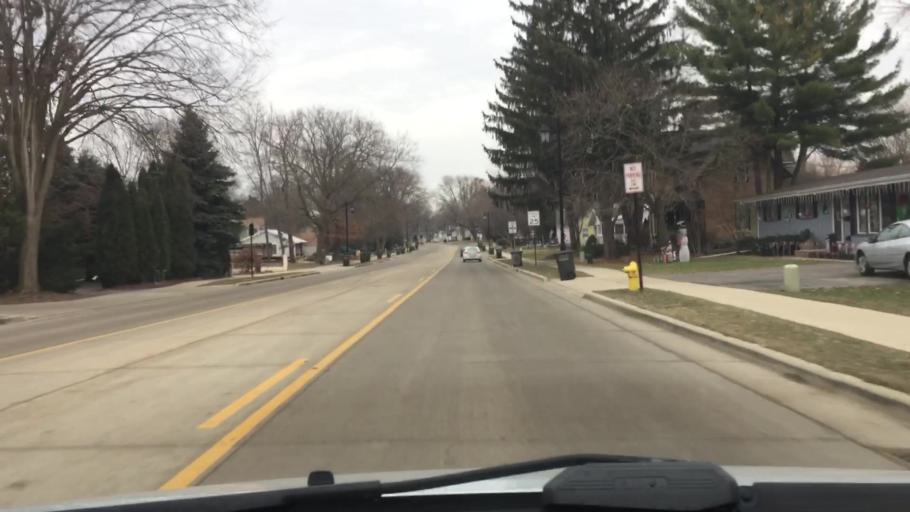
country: US
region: Wisconsin
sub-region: Waukesha County
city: Oconomowoc
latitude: 43.1179
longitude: -88.5185
